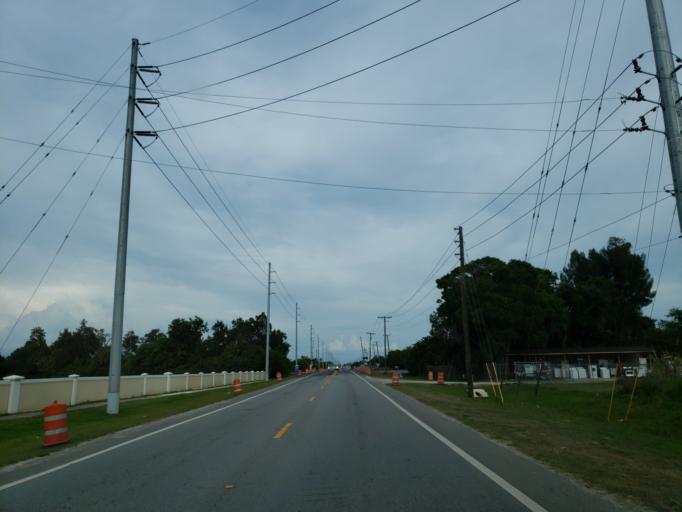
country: US
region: Florida
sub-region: Hillsborough County
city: Ruskin
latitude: 27.7350
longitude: -82.4136
